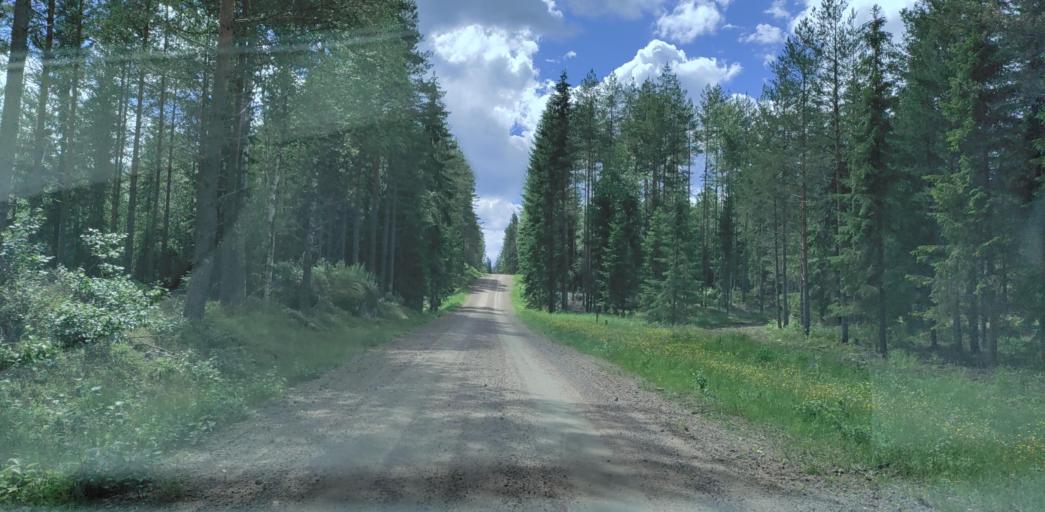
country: SE
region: Vaermland
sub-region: Hagfors Kommun
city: Ekshaerad
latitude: 60.1003
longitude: 13.3510
